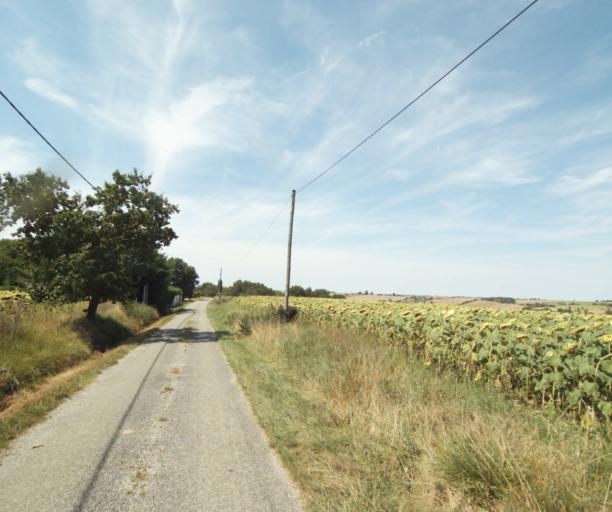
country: FR
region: Midi-Pyrenees
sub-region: Departement de la Haute-Garonne
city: Gaillac-Toulza
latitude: 43.2226
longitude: 1.4158
